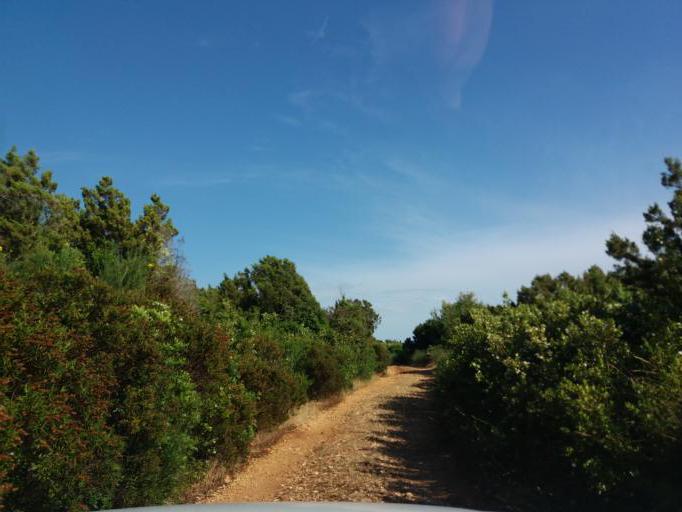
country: HR
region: Zadarska
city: Ugljan
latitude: 44.1276
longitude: 14.8673
